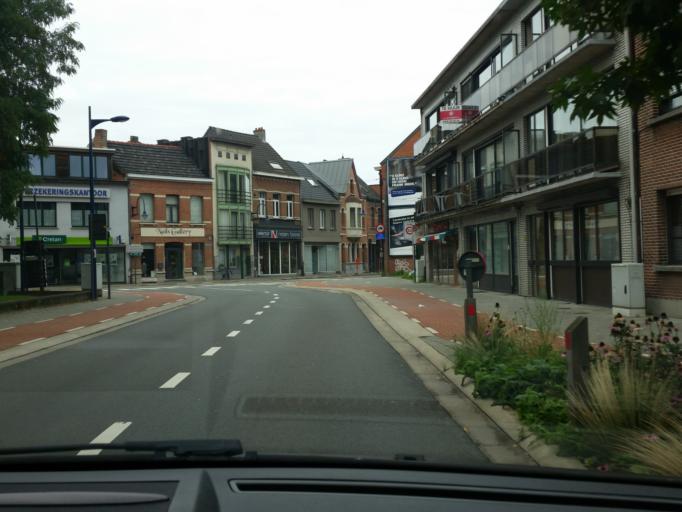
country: BE
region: Flanders
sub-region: Provincie Antwerpen
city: Kontich
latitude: 51.1318
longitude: 4.4471
